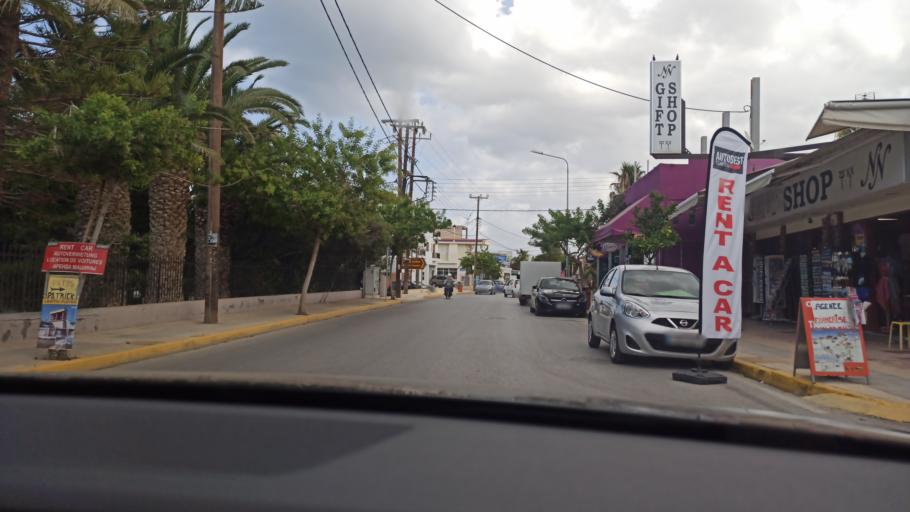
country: GR
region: Crete
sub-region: Nomos Irakleiou
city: Gazi
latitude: 35.3360
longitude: 25.0730
